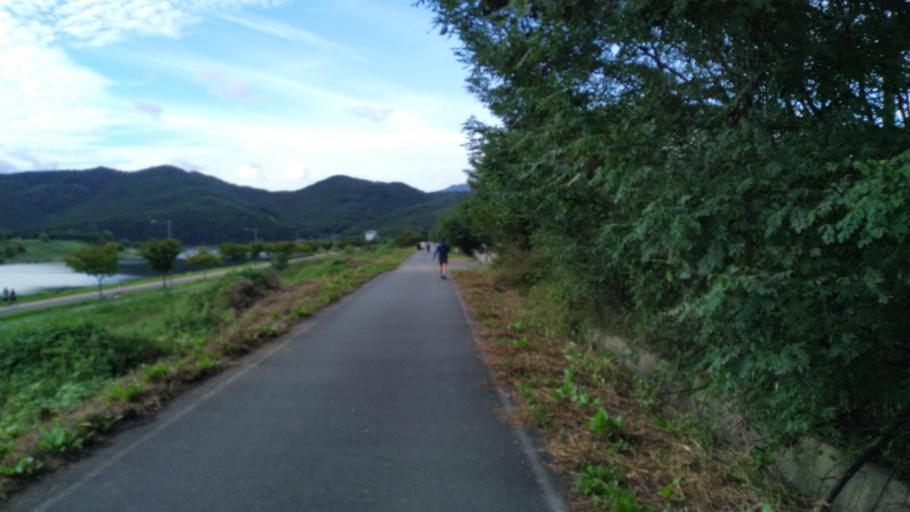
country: KR
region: Daegu
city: Daegu
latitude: 35.9200
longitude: 128.6333
